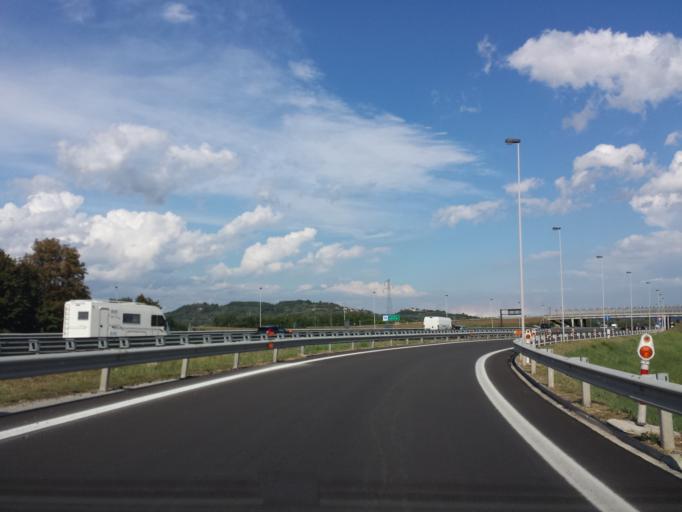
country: IT
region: Veneto
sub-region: Provincia di Vicenza
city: Gambellara
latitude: 45.4361
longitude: 11.3565
